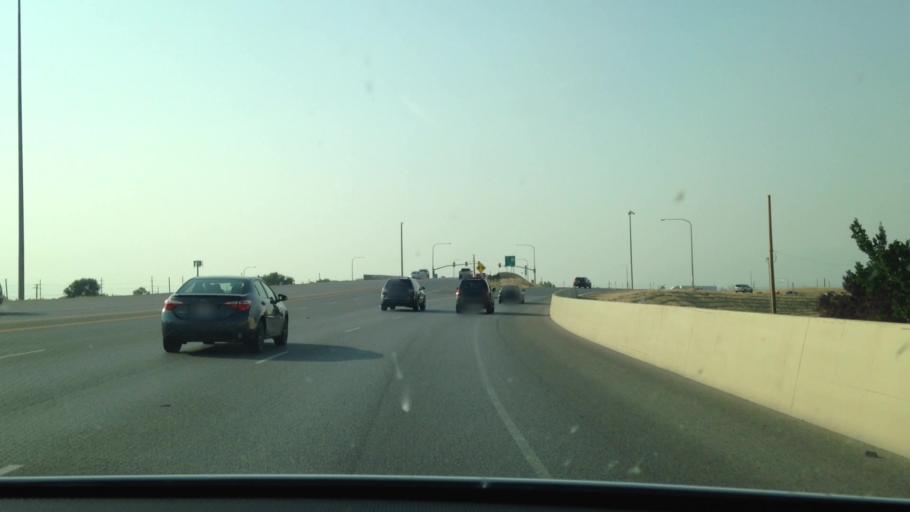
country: US
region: Utah
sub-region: Utah County
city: Spanish Fork
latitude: 40.1265
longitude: -111.6475
